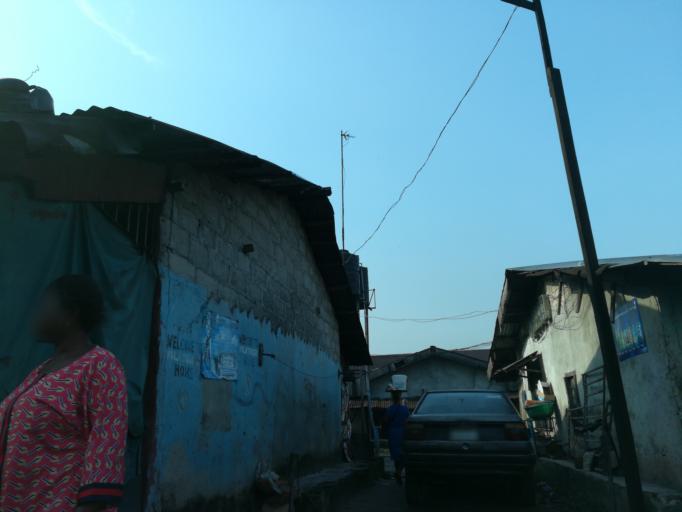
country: NG
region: Rivers
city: Port Harcourt
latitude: 4.8213
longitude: 7.0230
